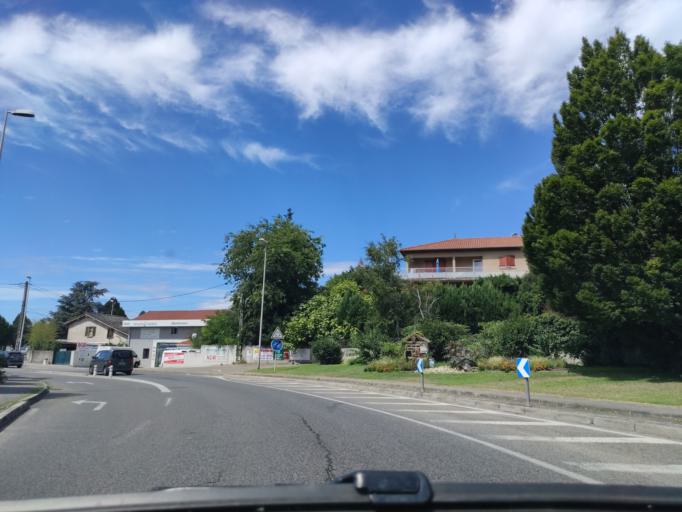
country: FR
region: Rhone-Alpes
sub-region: Departement de l'Isere
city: Le Peage-de-Roussillon
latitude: 45.3771
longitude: 4.7989
